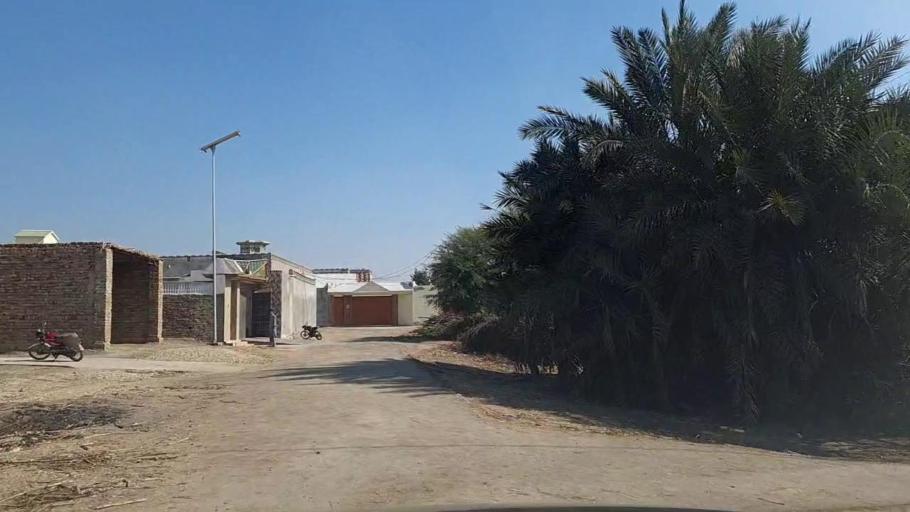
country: PK
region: Sindh
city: Bandhi
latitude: 26.5254
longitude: 68.3122
